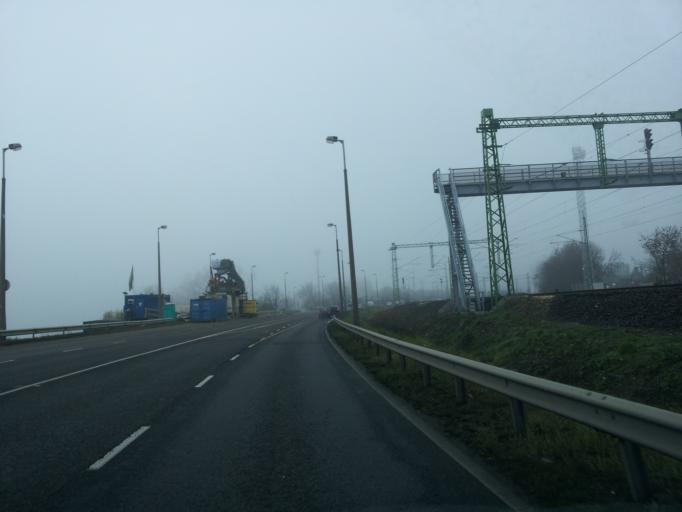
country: HU
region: Budapest
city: Budapest XXII. keruelet
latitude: 47.4157
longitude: 19.0418
